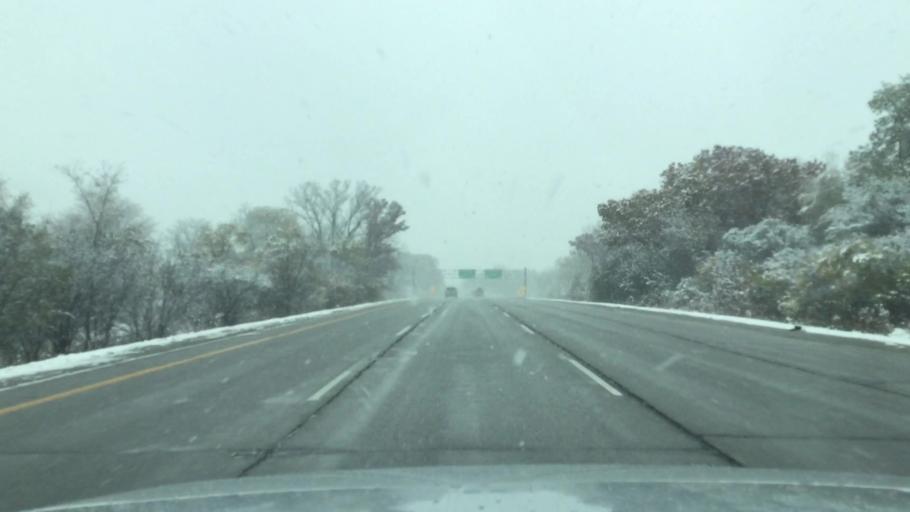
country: US
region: Michigan
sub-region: Oakland County
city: Bloomfield Hills
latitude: 42.6080
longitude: -83.2393
